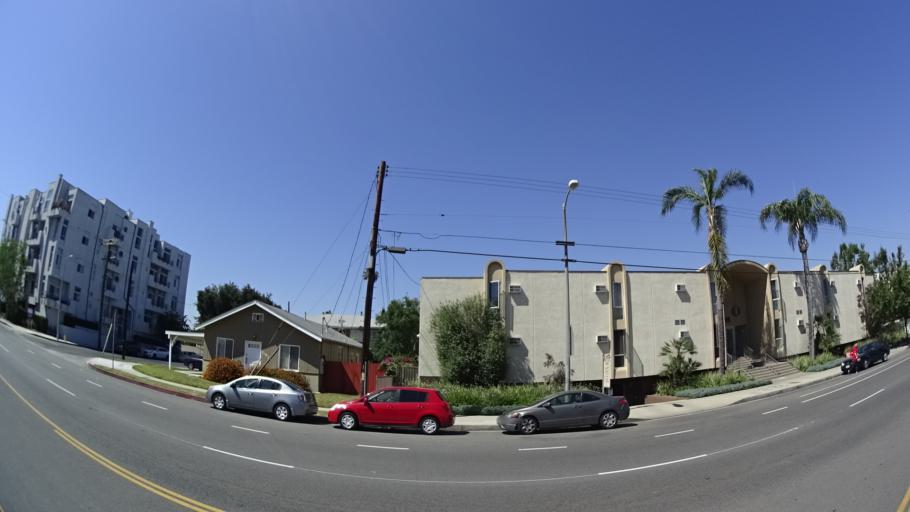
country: US
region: California
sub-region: Los Angeles County
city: North Hollywood
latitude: 34.1721
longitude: -118.3929
